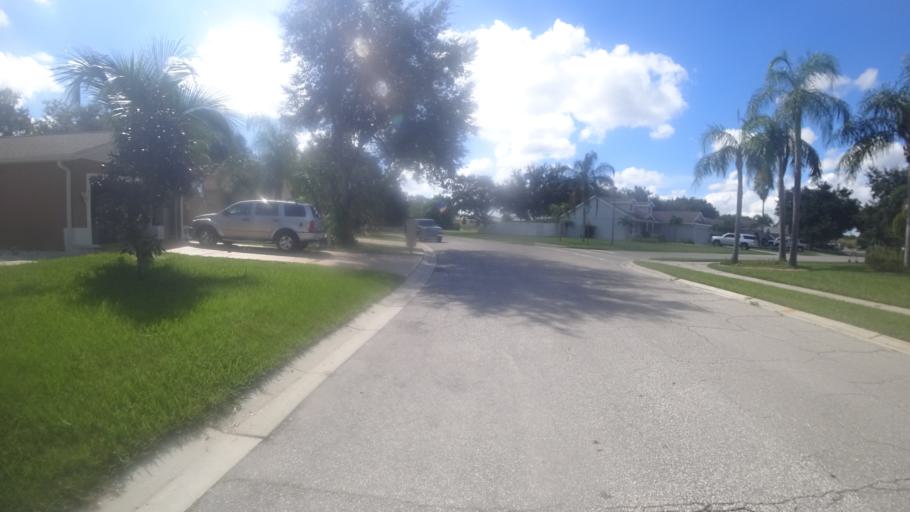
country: US
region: Florida
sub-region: Manatee County
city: Ellenton
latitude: 27.4958
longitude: -82.4305
